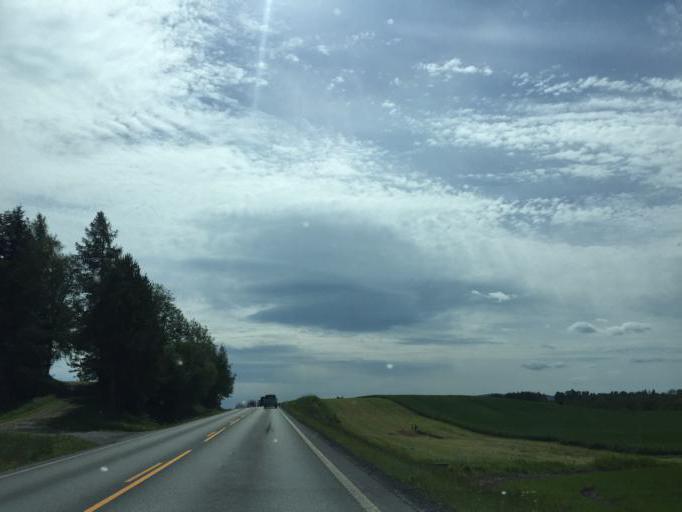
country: NO
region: Akershus
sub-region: Nes
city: Arnes
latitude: 60.1309
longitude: 11.4406
